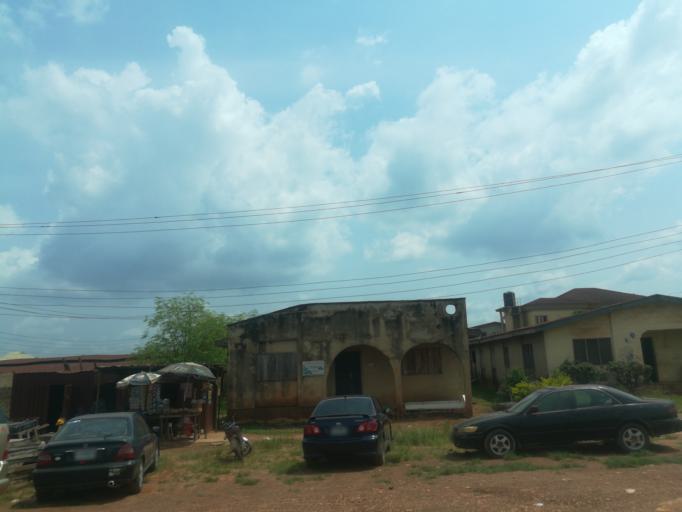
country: NG
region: Oyo
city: Moniya
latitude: 7.4547
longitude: 3.9501
